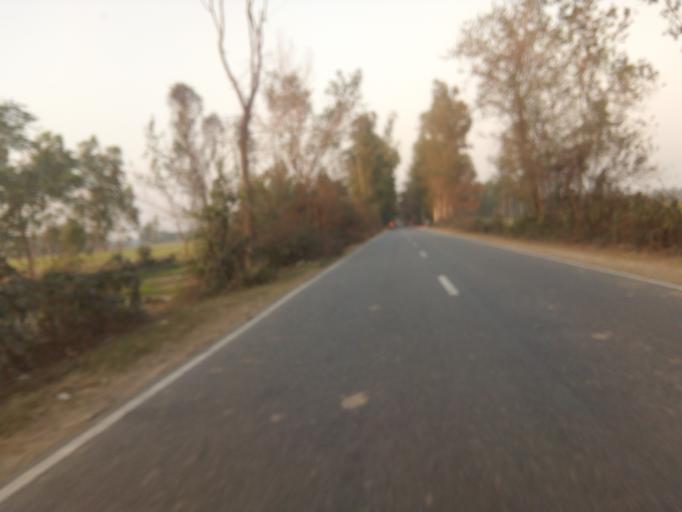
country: BD
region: Rajshahi
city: Bogra
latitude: 24.6292
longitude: 89.2449
